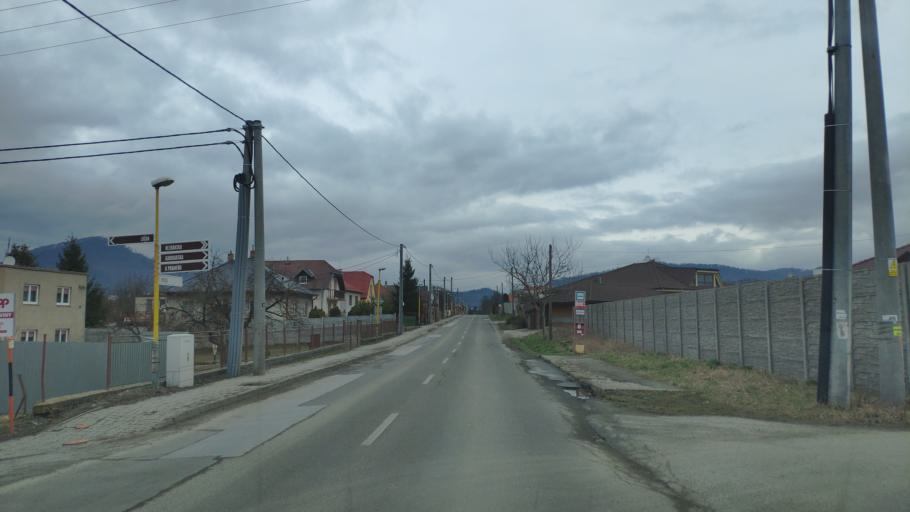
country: SK
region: Presovsky
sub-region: Okres Presov
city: Presov
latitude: 49.0274
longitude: 21.2797
